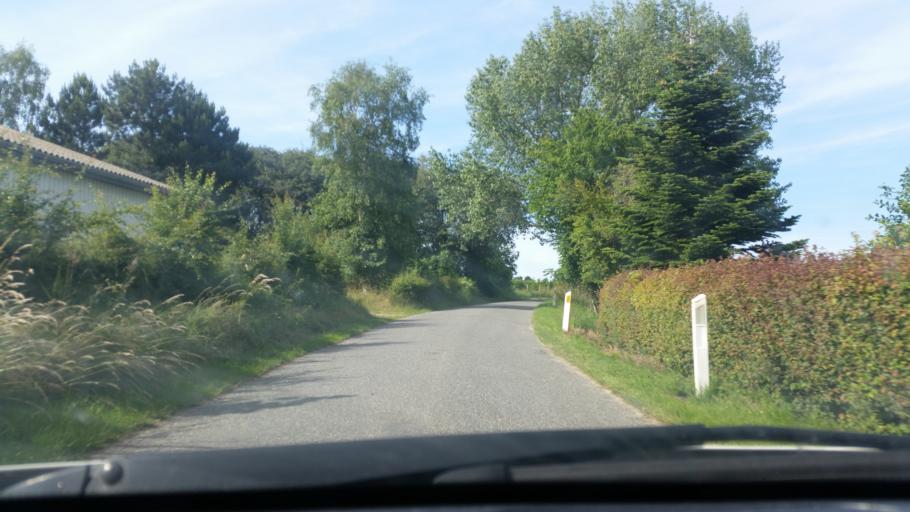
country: DK
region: Central Jutland
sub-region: Samso Kommune
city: Tranebjerg
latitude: 55.7855
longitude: 10.5536
